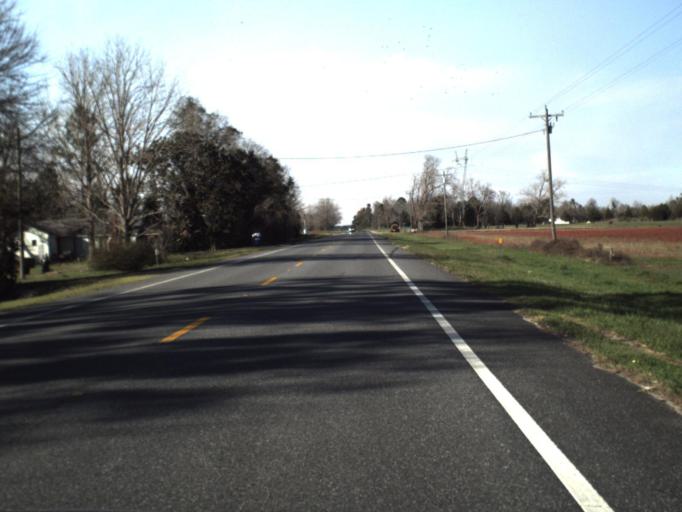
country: US
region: Florida
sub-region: Calhoun County
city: Blountstown
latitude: 30.4855
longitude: -85.2002
